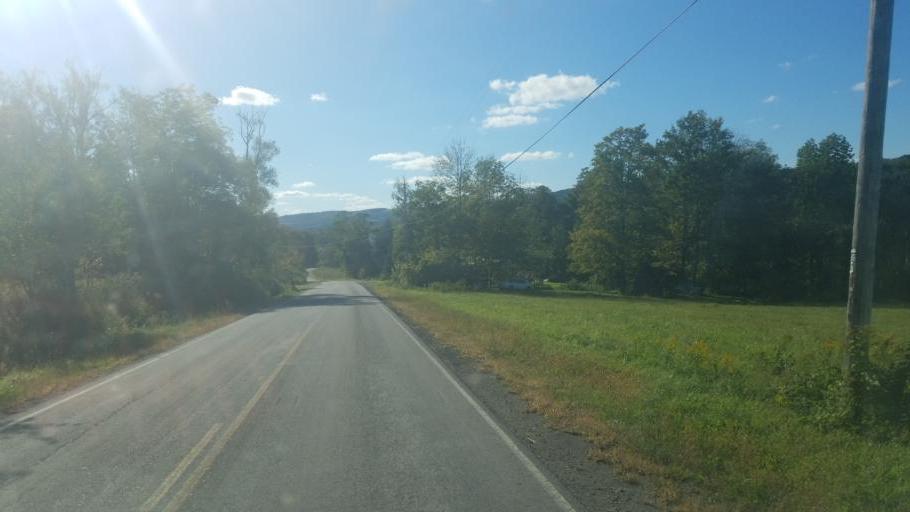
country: US
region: New York
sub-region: Allegany County
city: Friendship
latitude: 42.2756
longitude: -78.1956
